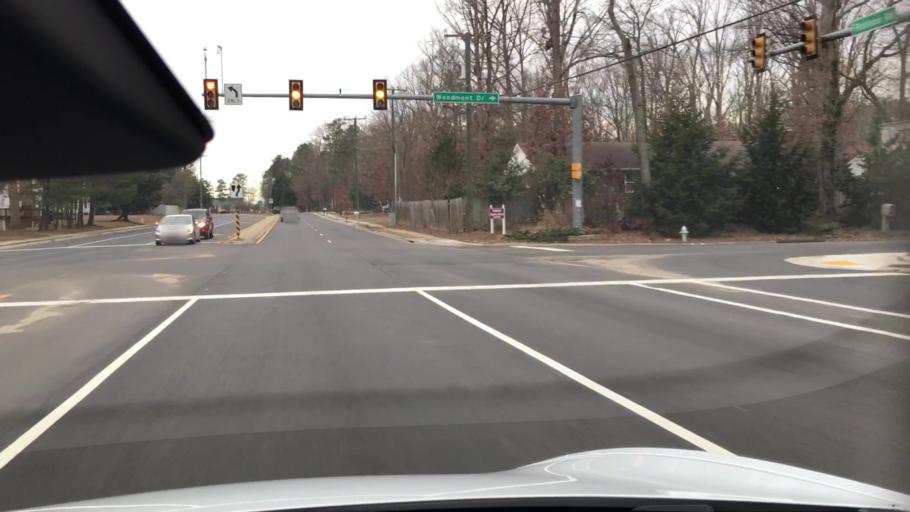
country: US
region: Virginia
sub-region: Chesterfield County
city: Bon Air
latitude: 37.5175
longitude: -77.5982
